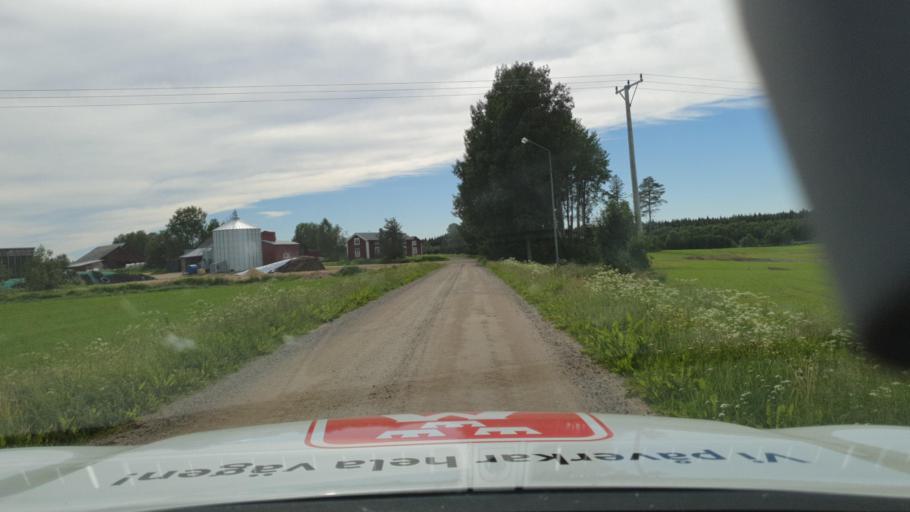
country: SE
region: Vaesterbotten
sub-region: Robertsfors Kommun
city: Robertsfors
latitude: 64.3835
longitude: 21.0395
